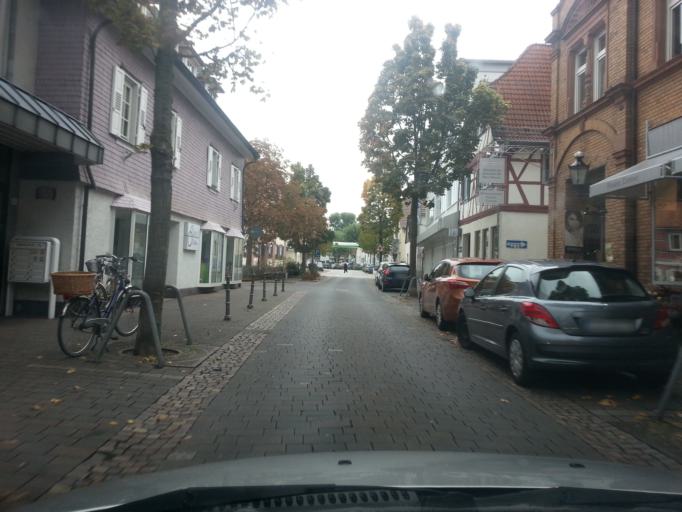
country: DE
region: Hesse
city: Lorsch
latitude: 49.6548
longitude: 8.5675
